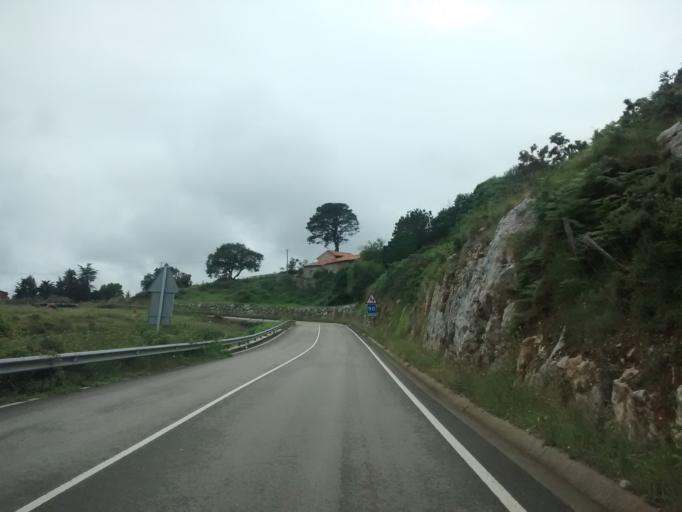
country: ES
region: Cantabria
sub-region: Provincia de Cantabria
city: Santillana
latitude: 43.4086
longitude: -4.1068
